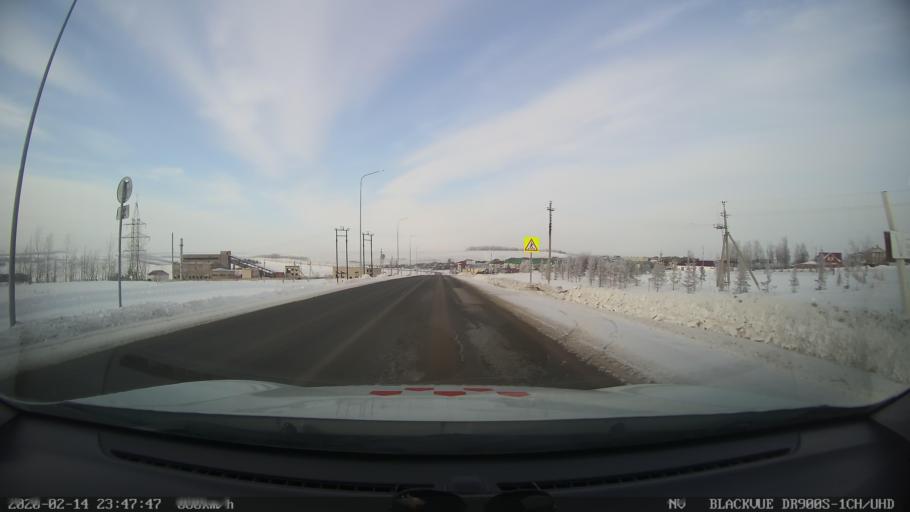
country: RU
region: Tatarstan
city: Kuybyshevskiy Zaton
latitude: 55.2426
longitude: 49.2069
